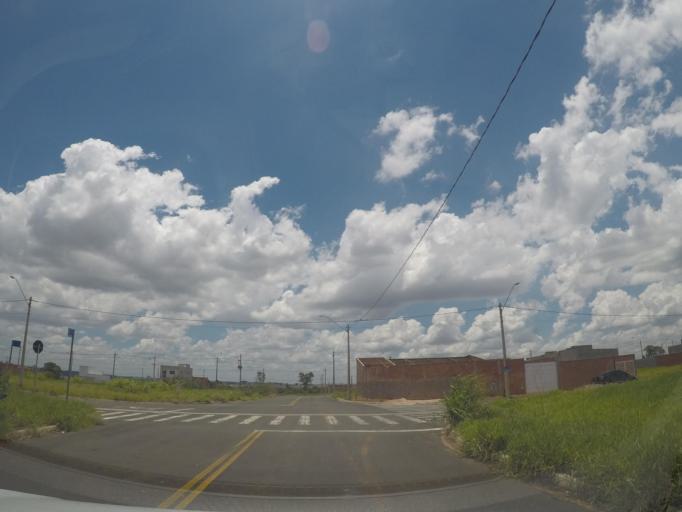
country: BR
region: Sao Paulo
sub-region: Hortolandia
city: Hortolandia
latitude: -22.8394
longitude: -47.2193
